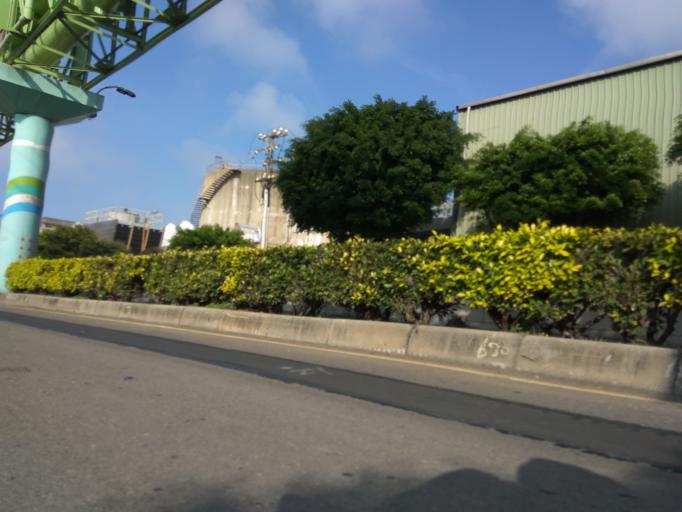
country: TW
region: Taiwan
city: Taoyuan City
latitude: 25.0721
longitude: 121.1775
